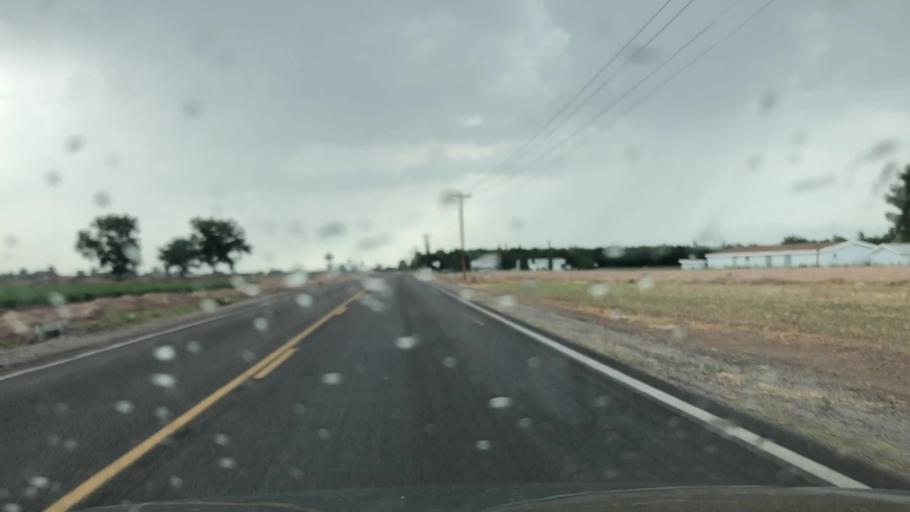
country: US
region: New Mexico
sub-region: Dona Ana County
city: Vado
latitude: 32.0732
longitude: -106.6835
